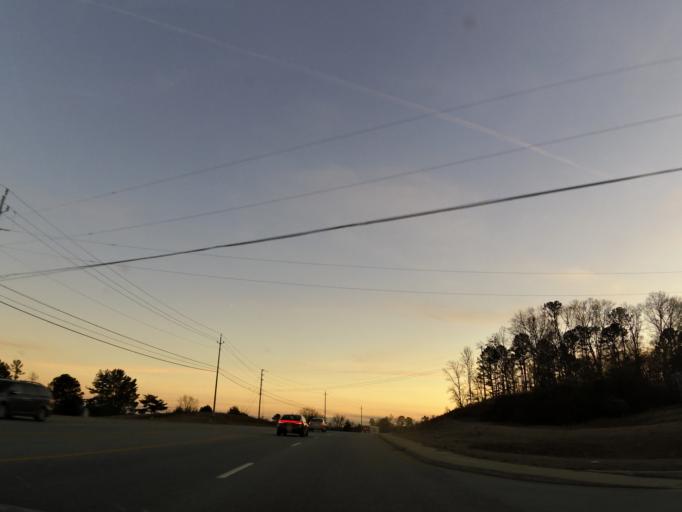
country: US
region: Tennessee
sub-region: Bradley County
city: Wildwood Lake
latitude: 35.1110
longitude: -84.8627
